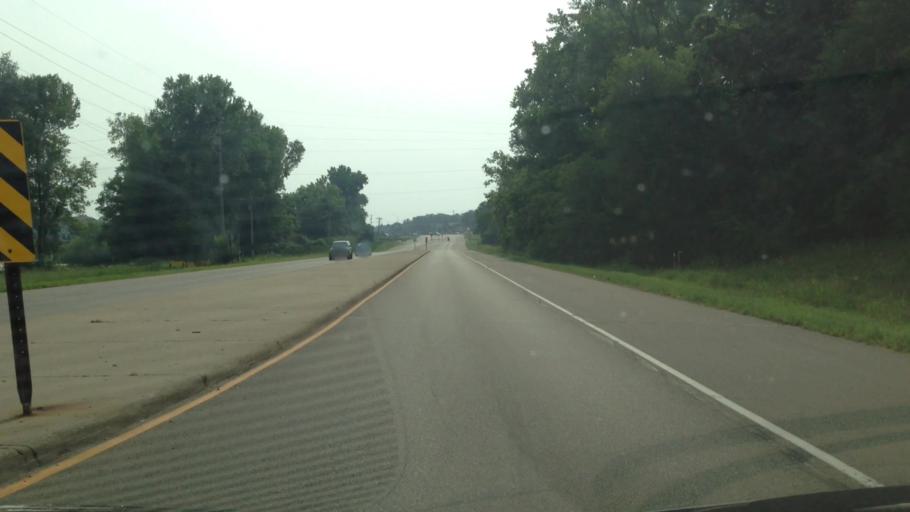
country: US
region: Minnesota
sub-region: Anoka County
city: Lexington
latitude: 45.1442
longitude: -93.1576
